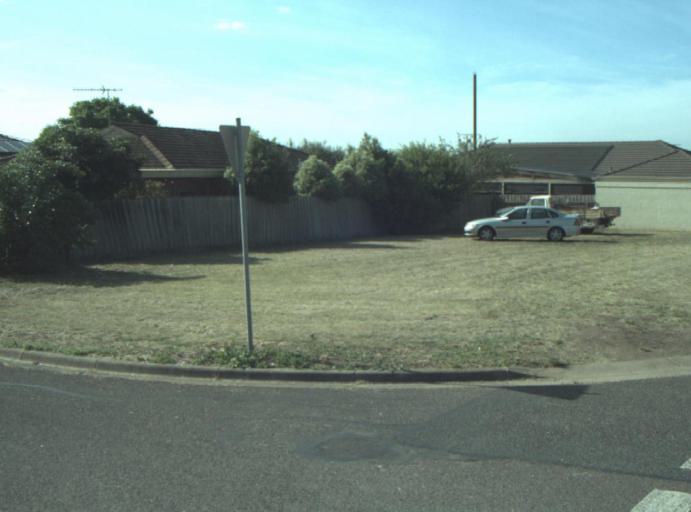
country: AU
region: Victoria
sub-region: Greater Geelong
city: Hamlyn Heights
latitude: -38.1189
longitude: 144.3218
